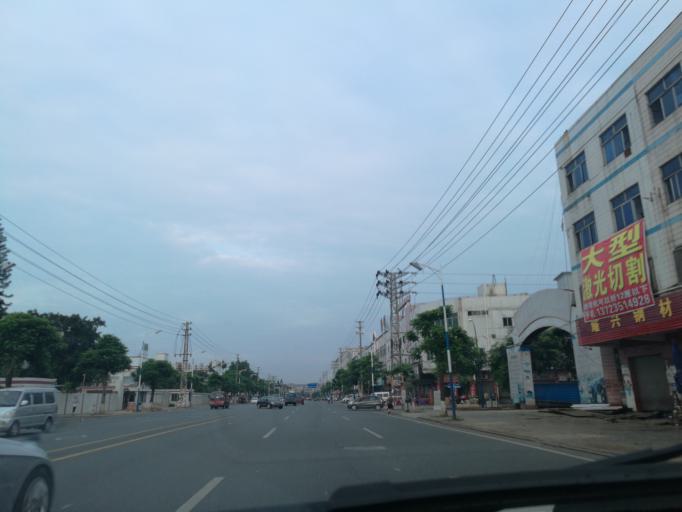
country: CN
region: Guangdong
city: Hengli
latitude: 23.0243
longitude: 113.9834
